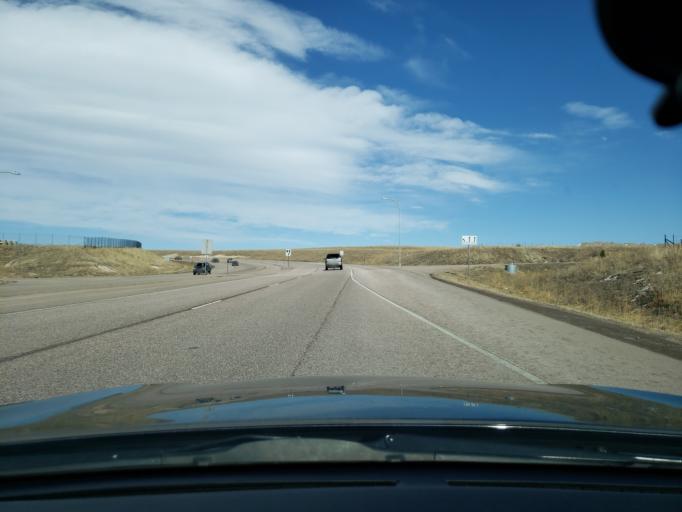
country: US
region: Colorado
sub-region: El Paso County
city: Gleneagle
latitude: 39.0012
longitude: -104.7776
